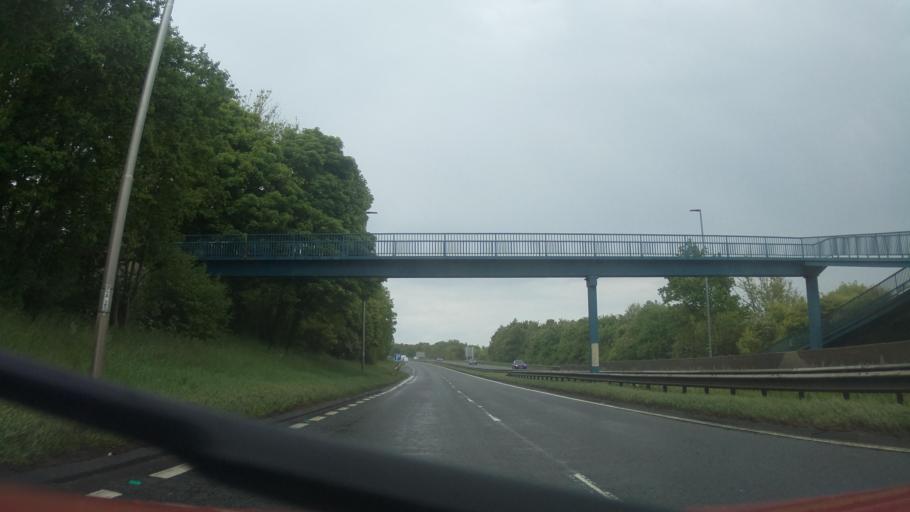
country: GB
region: England
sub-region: County Durham
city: Hawthorn
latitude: 54.8209
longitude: -1.3698
